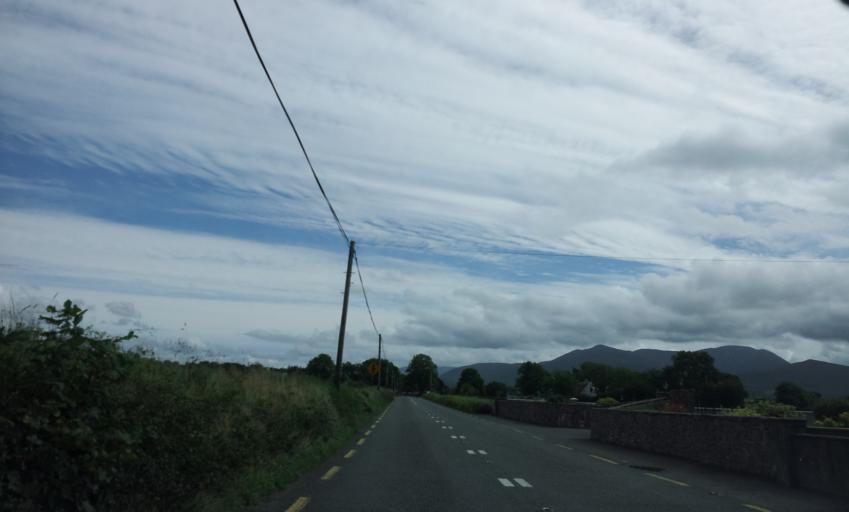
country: IE
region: Munster
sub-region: Ciarrai
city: Killorglin
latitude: 52.0897
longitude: -9.6883
